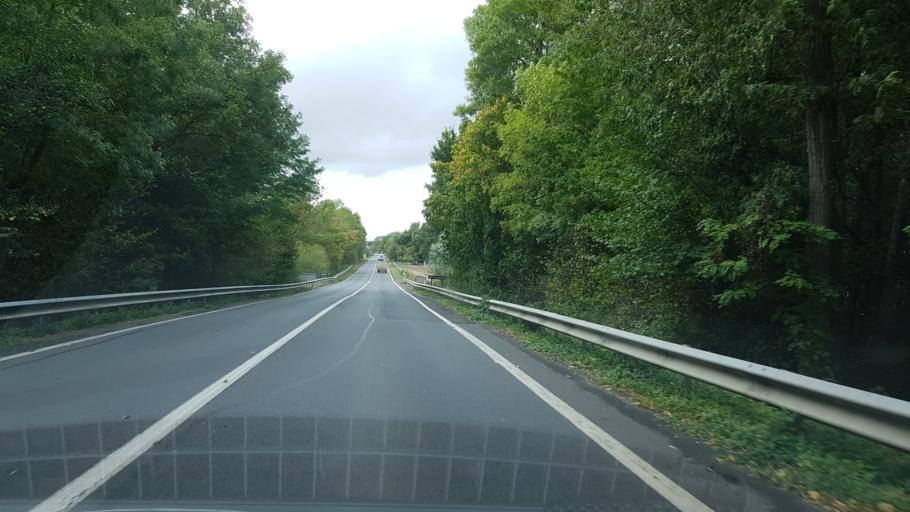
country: FR
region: Centre
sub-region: Departement du Loiret
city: Saint-Maurice-sur-Fessard
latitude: 47.9888
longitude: 2.6375
